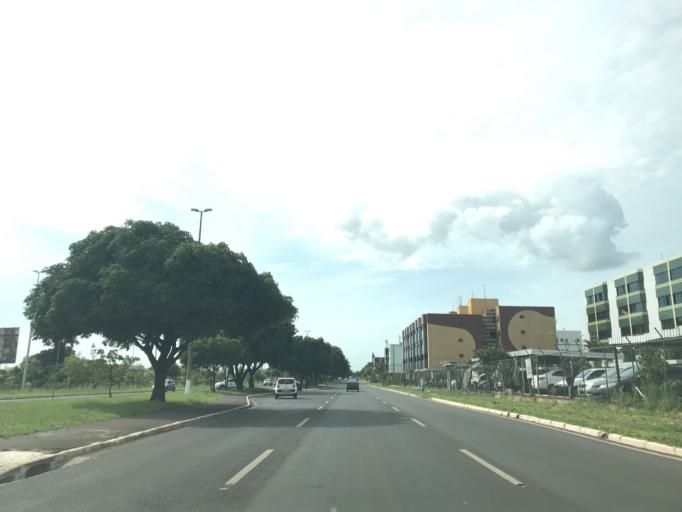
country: BR
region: Federal District
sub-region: Brasilia
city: Brasilia
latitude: -15.8214
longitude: -48.0864
